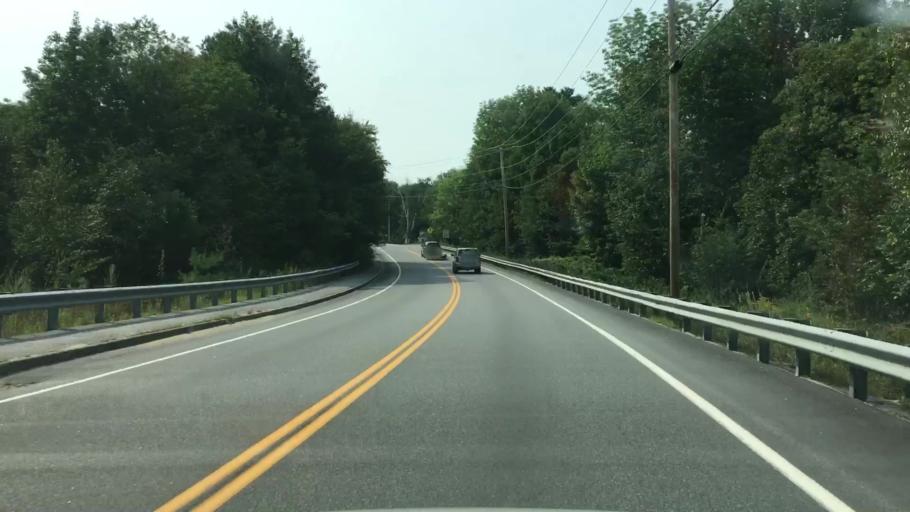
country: US
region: Maine
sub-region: Oxford County
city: Buckfield
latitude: 44.2860
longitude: -70.3556
